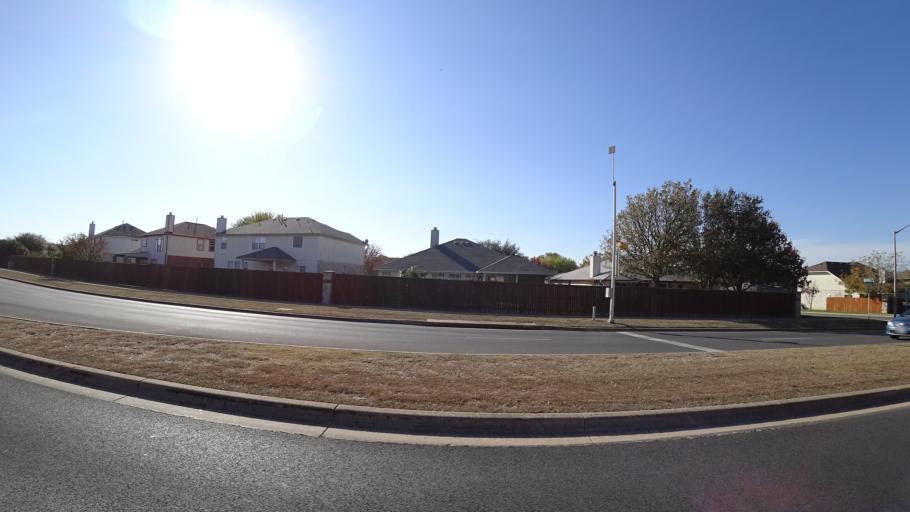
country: US
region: Texas
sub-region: Williamson County
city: Cedar Park
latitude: 30.5236
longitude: -97.8539
